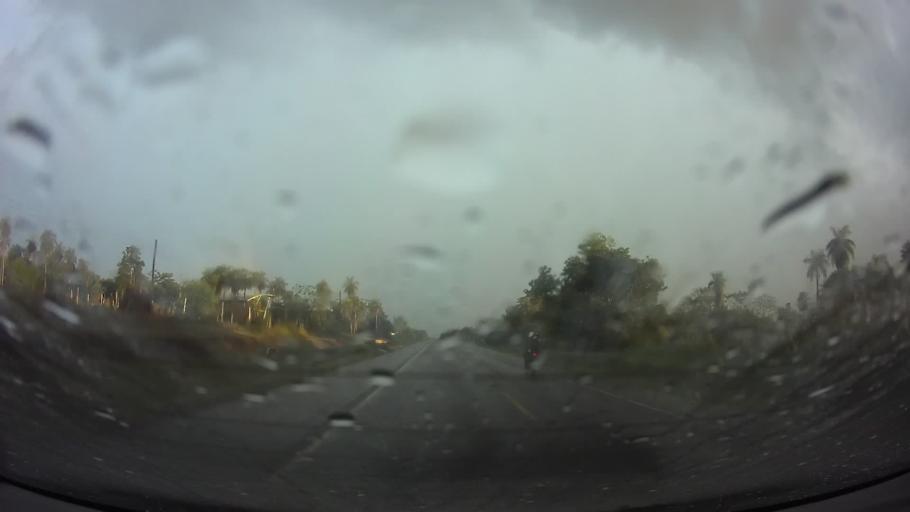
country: PY
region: Paraguari
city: Paraguari
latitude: -25.6183
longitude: -57.1744
